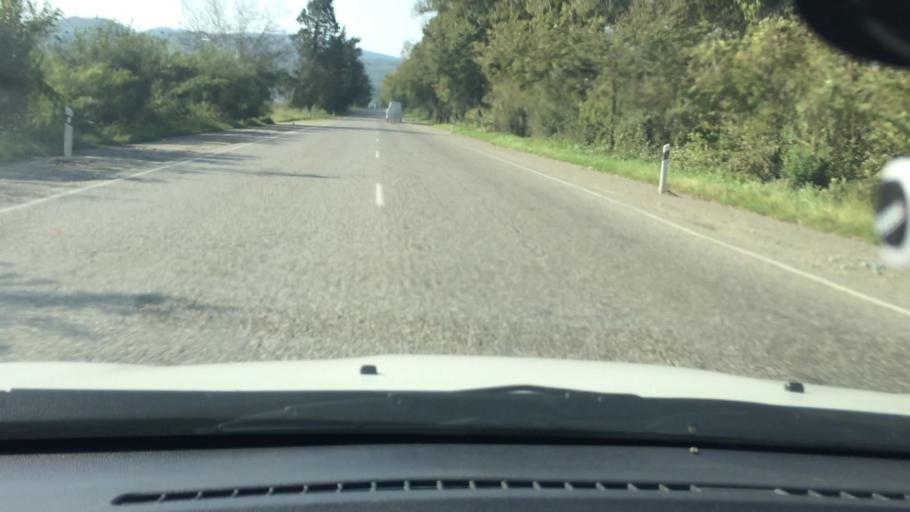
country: GE
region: Imereti
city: Samtredia
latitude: 42.1241
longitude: 42.3340
